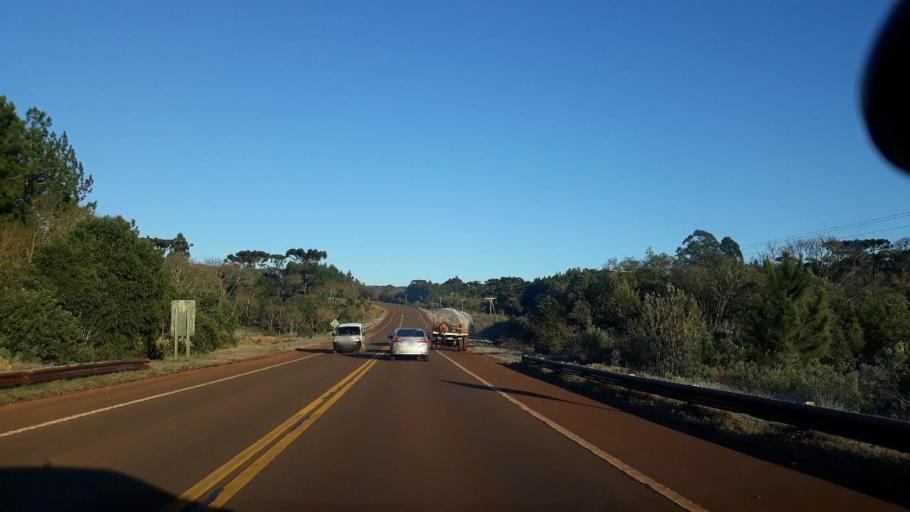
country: AR
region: Misiones
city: San Vicente
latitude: -26.6370
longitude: -54.1325
